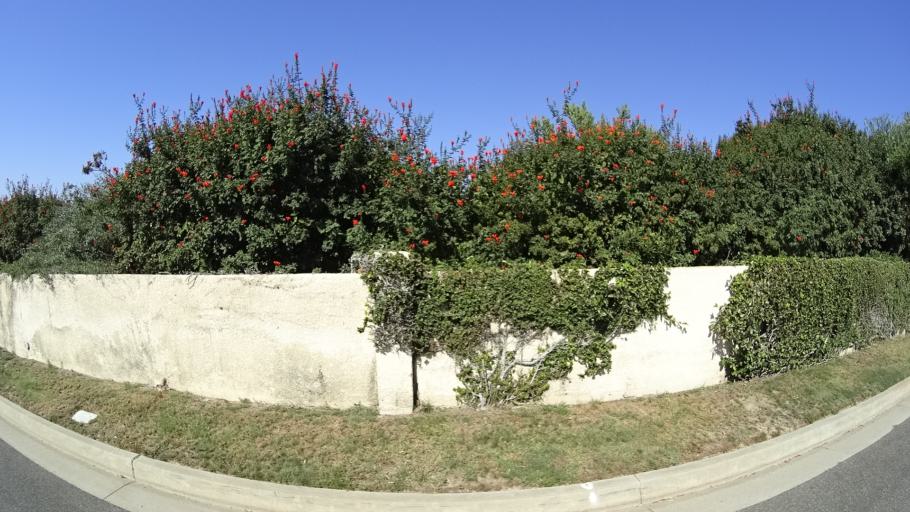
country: US
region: California
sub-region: Orange County
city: San Clemente
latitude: 33.4483
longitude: -117.6277
